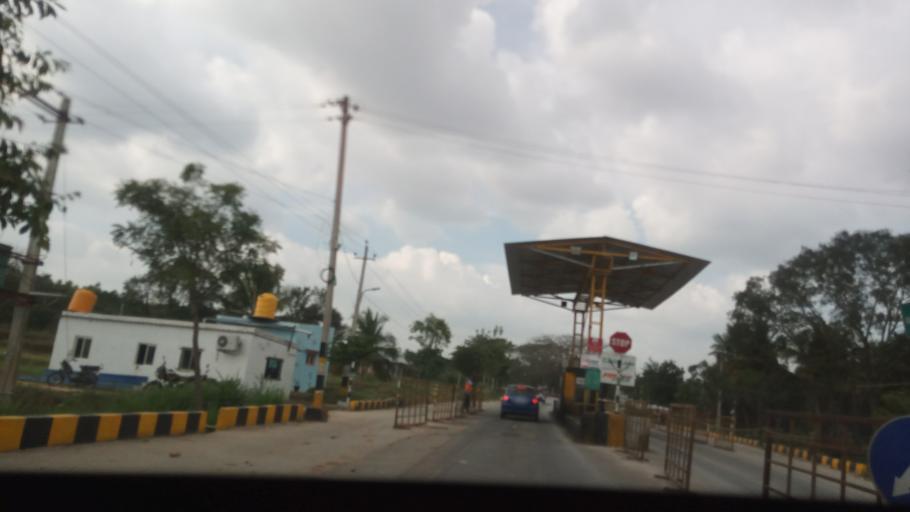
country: IN
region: Karnataka
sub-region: Tumkur
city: Kunigal
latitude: 12.8928
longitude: 77.0446
